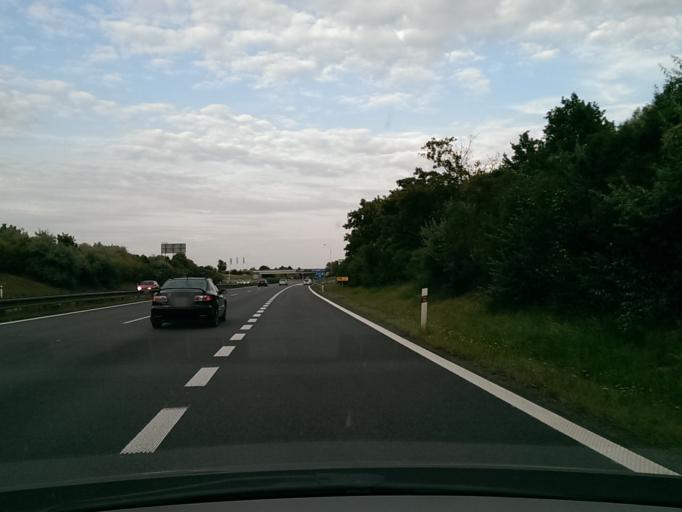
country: CZ
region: South Moravian
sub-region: Mesto Brno
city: Brno
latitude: 49.1630
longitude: 16.6566
